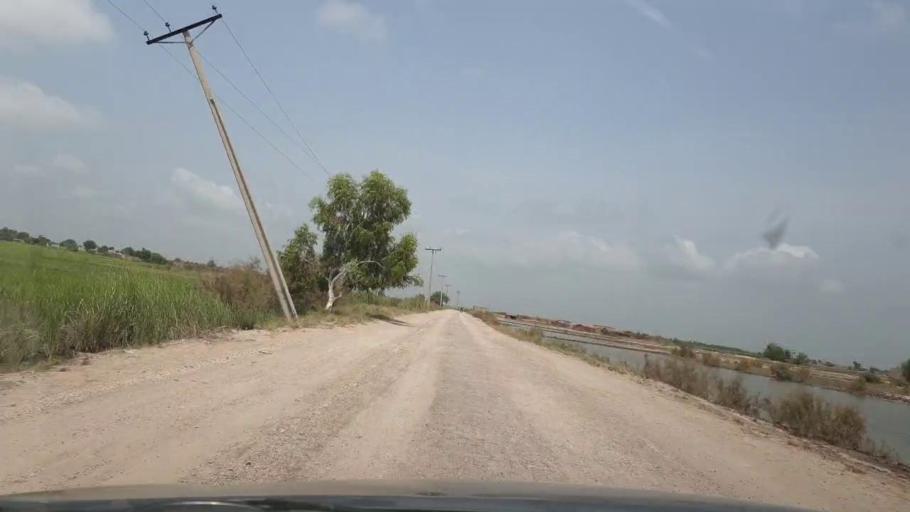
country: PK
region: Sindh
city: Ratodero
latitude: 27.9072
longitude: 68.3111
